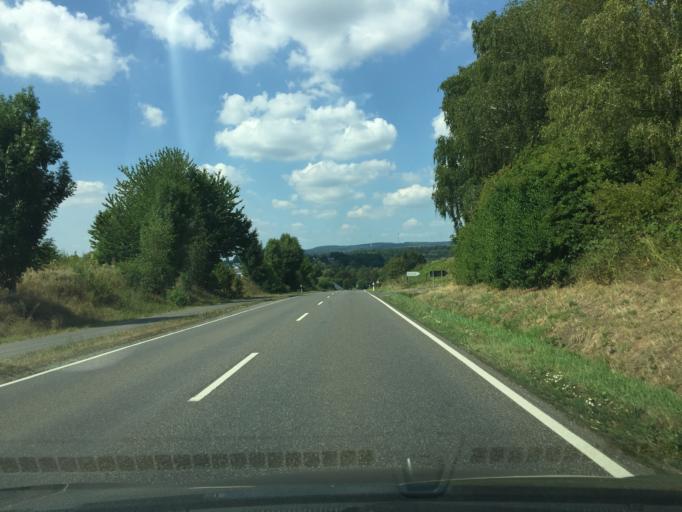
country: DE
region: Hesse
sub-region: Regierungsbezirk Giessen
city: Elz
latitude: 50.4650
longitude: 8.0485
